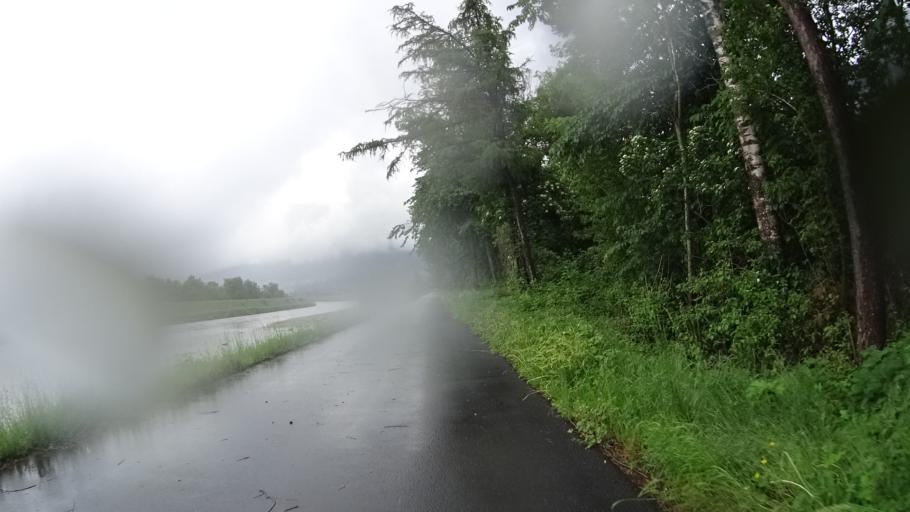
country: LI
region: Balzers
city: Balzers
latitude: 47.0818
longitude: 9.5083
